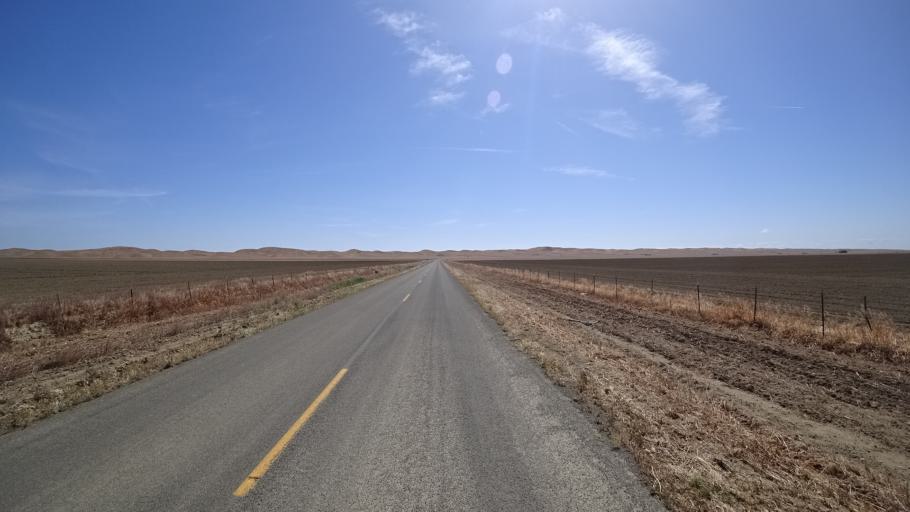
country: US
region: California
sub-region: Kings County
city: Kettleman City
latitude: 35.9352
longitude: -120.0352
